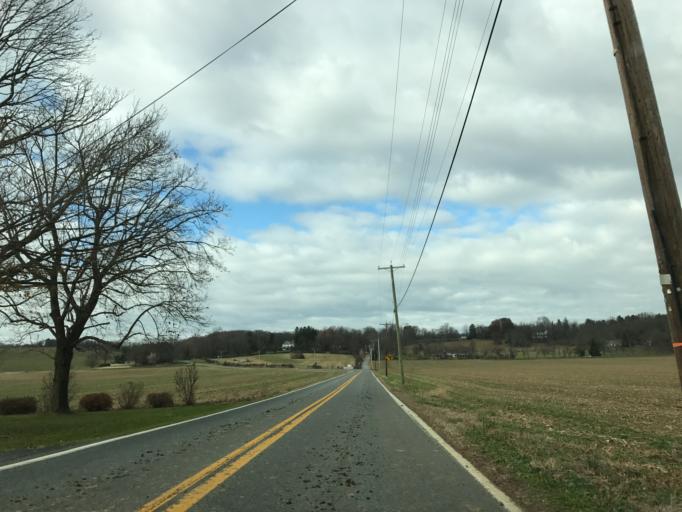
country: US
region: Maryland
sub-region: Baltimore County
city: Perry Hall
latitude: 39.4847
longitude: -76.4944
